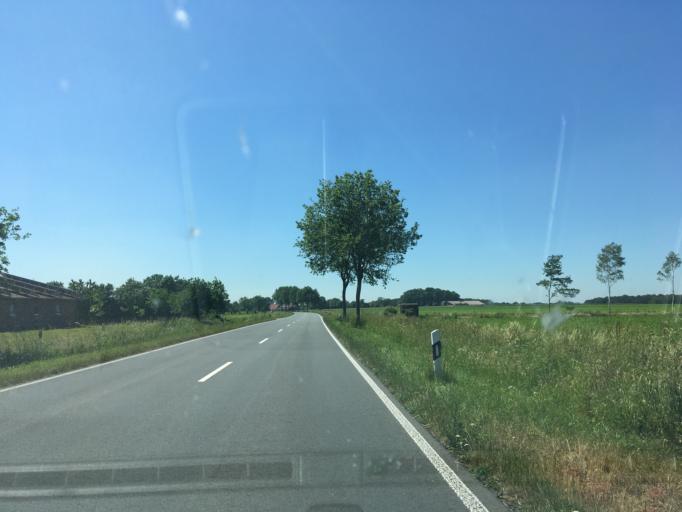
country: DE
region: North Rhine-Westphalia
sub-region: Regierungsbezirk Munster
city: Raesfeld
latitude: 51.7969
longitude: 6.8139
